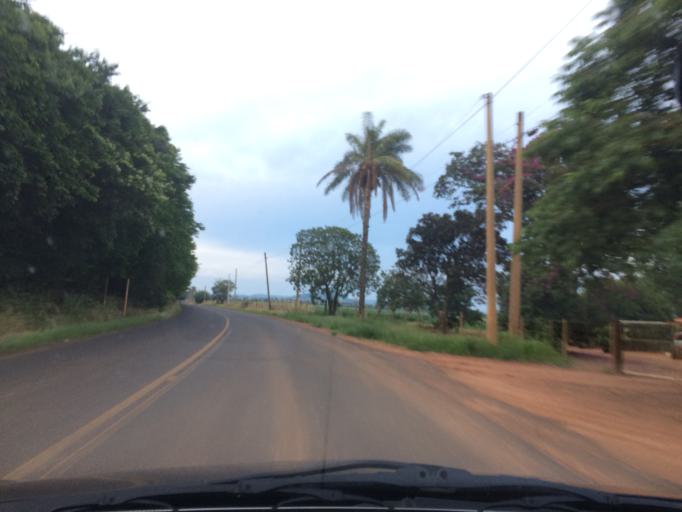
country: BR
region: Sao Paulo
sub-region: Casa Branca
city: Casa Branca
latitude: -21.7407
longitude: -47.1742
